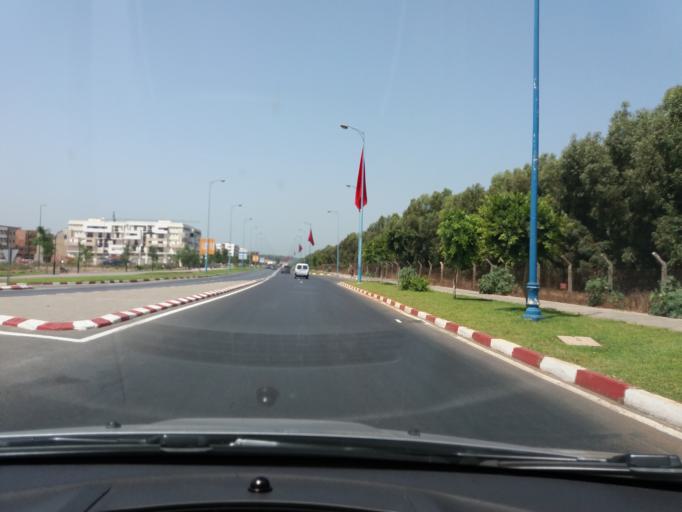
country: MA
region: Gharb-Chrarda-Beni Hssen
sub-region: Kenitra Province
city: Kenitra
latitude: 34.2730
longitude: -6.6215
